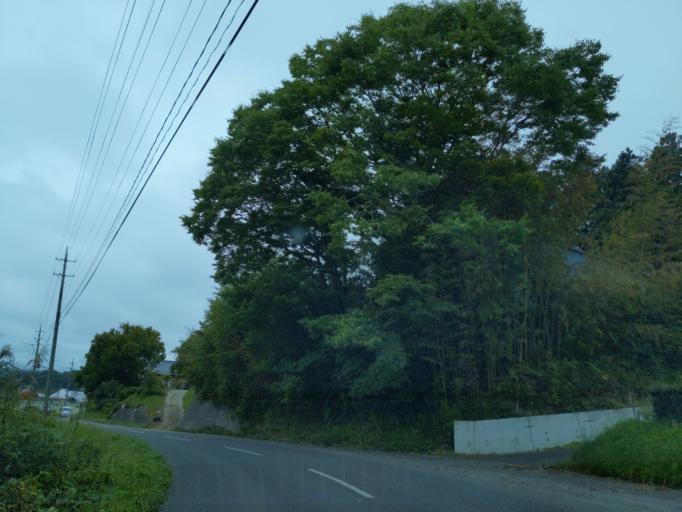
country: JP
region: Fukushima
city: Funehikimachi-funehiki
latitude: 37.4253
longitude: 140.6056
